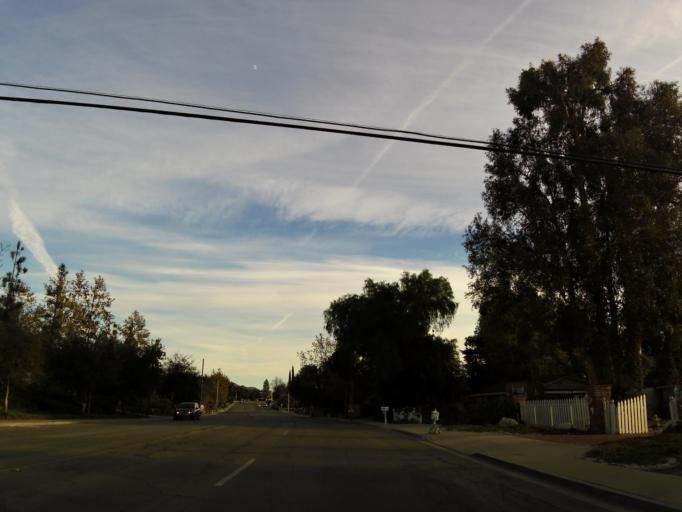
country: US
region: California
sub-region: Ventura County
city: Thousand Oaks
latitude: 34.1756
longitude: -118.8382
